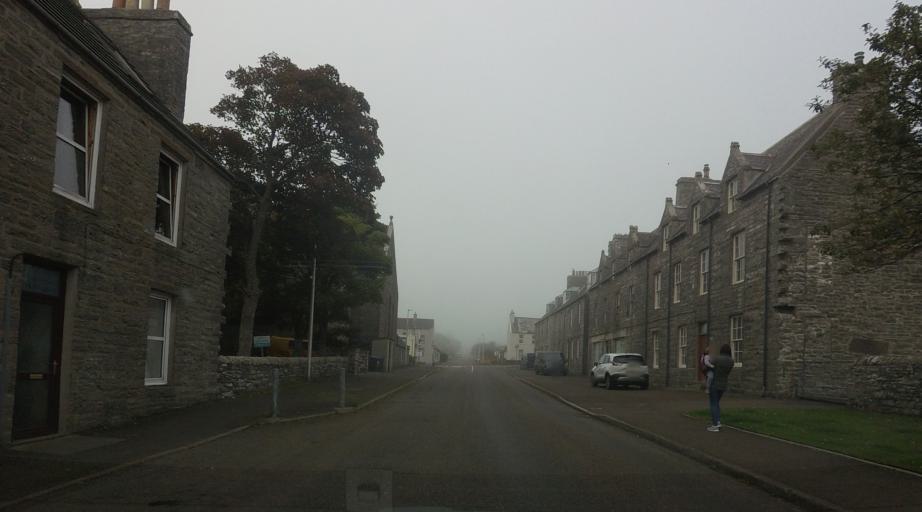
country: GB
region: Scotland
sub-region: Highland
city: Wick
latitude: 58.3076
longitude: -3.2857
